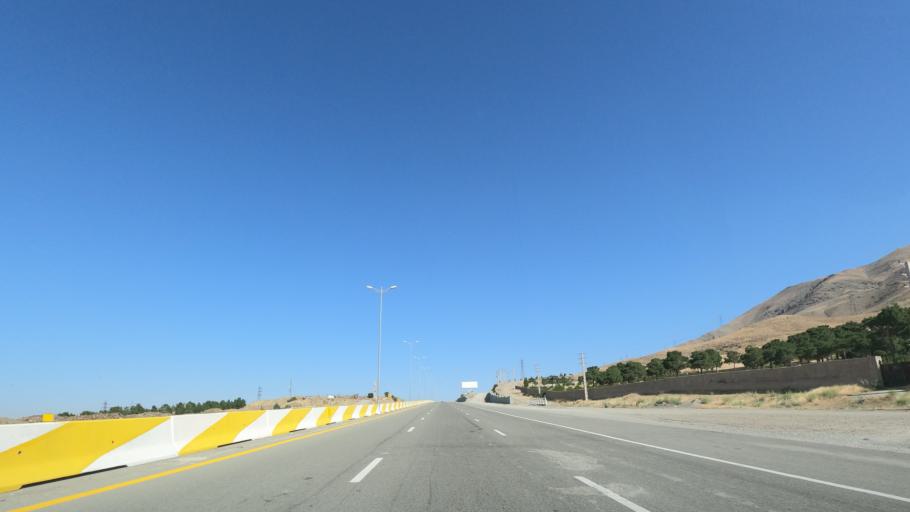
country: IR
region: Tehran
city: Shahr-e Qods
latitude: 35.7638
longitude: 51.0710
